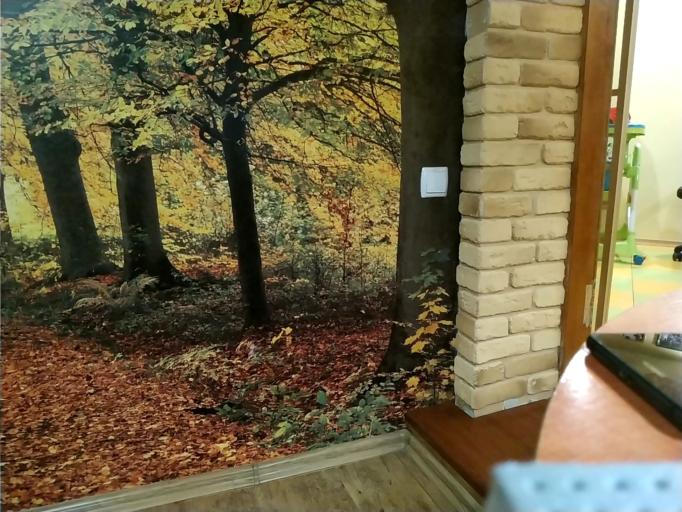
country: RU
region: Tverskaya
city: Zubtsov
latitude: 56.2480
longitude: 34.7015
